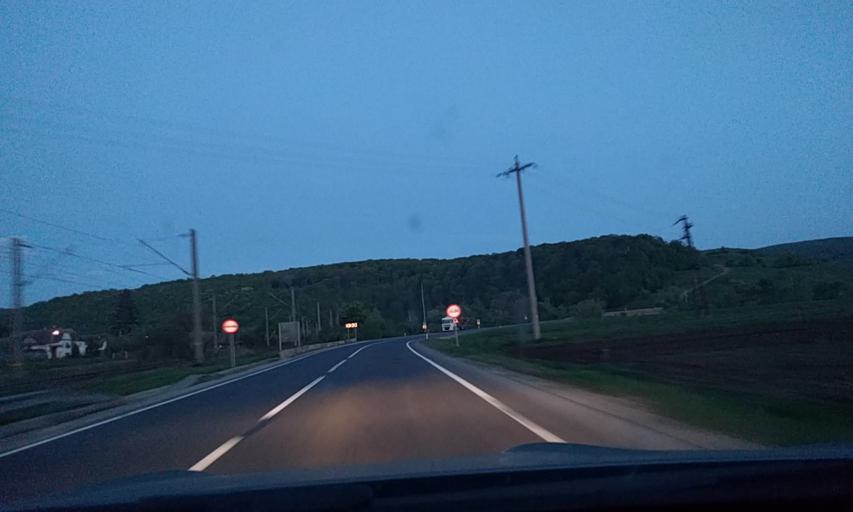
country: RO
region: Mures
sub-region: Comuna Vanatori
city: Vanatori
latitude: 46.2294
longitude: 24.9779
